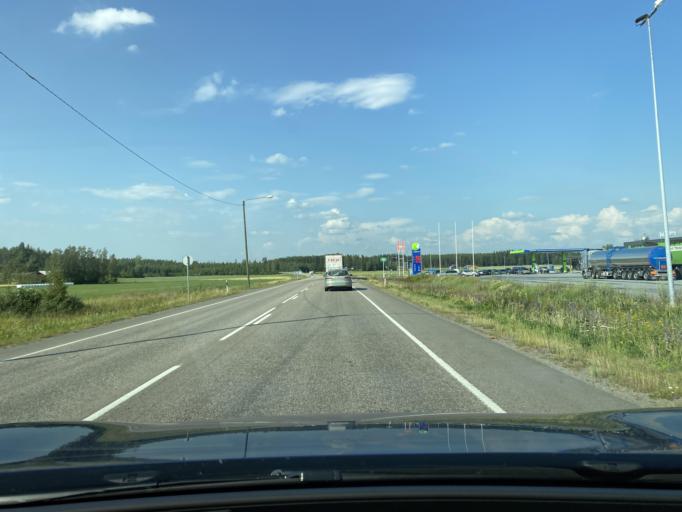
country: FI
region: Southern Ostrobothnia
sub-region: Seinaejoki
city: Jalasjaervi
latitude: 62.5105
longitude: 22.7274
